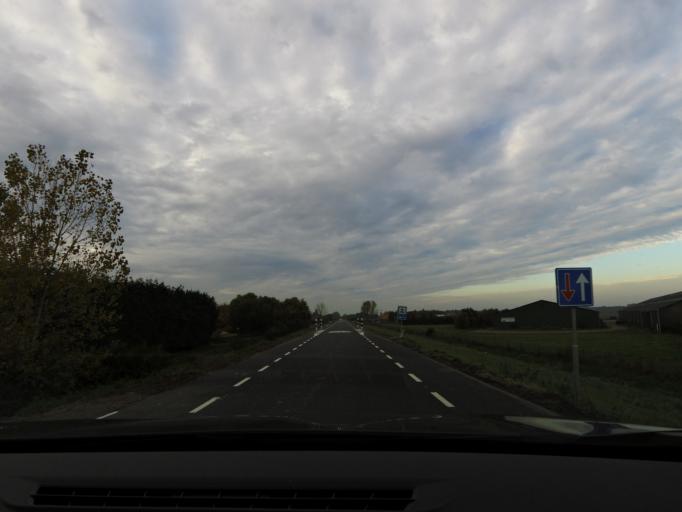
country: NL
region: South Holland
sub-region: Gemeente Goeree-Overflakkee
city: Goedereede
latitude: 51.7991
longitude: 4.0350
